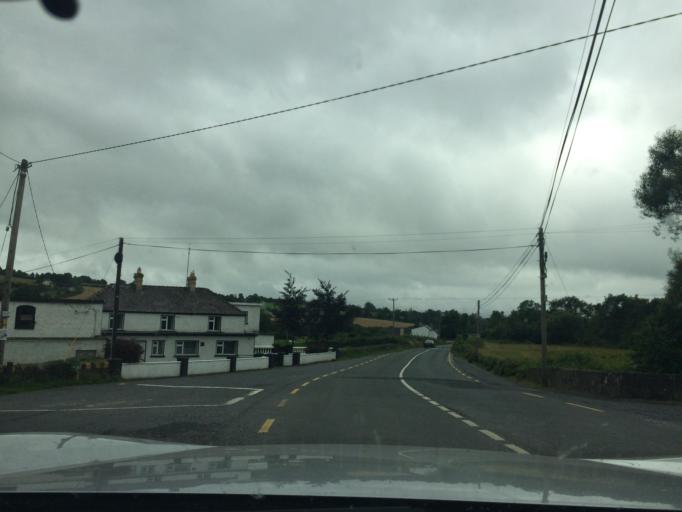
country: IE
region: Munster
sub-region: South Tipperary
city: Cluain Meala
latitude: 52.3169
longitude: -7.7768
